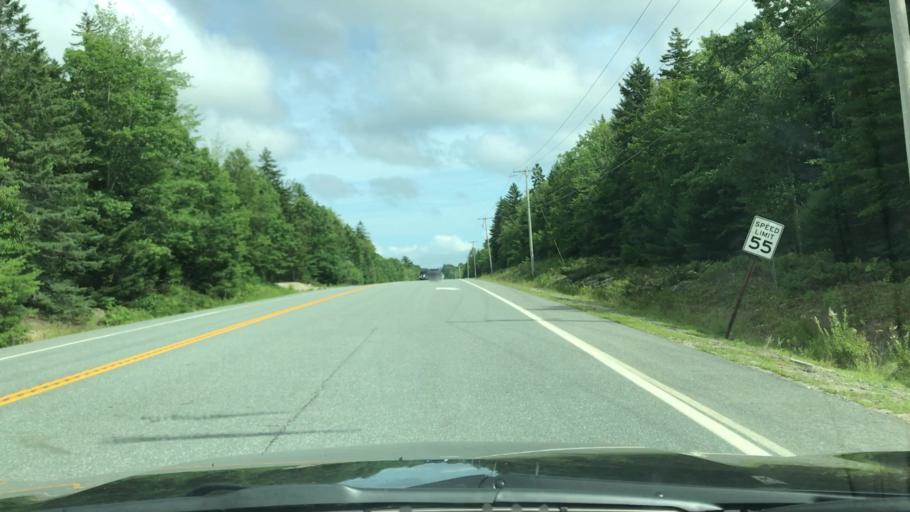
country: US
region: Maine
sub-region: Hancock County
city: Surry
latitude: 44.5535
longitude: -68.5369
